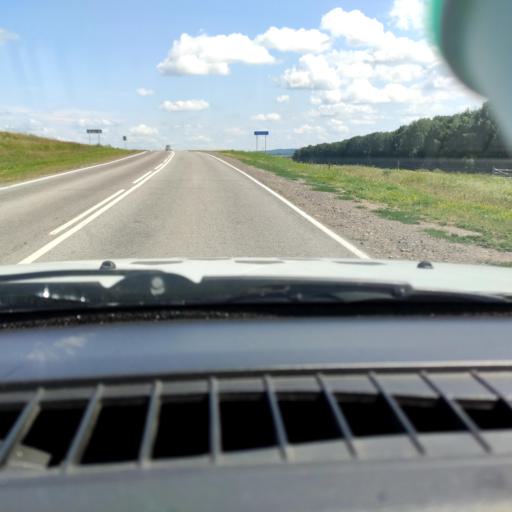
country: RU
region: Bashkortostan
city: Mesyagutovo
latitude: 55.4586
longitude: 58.3930
